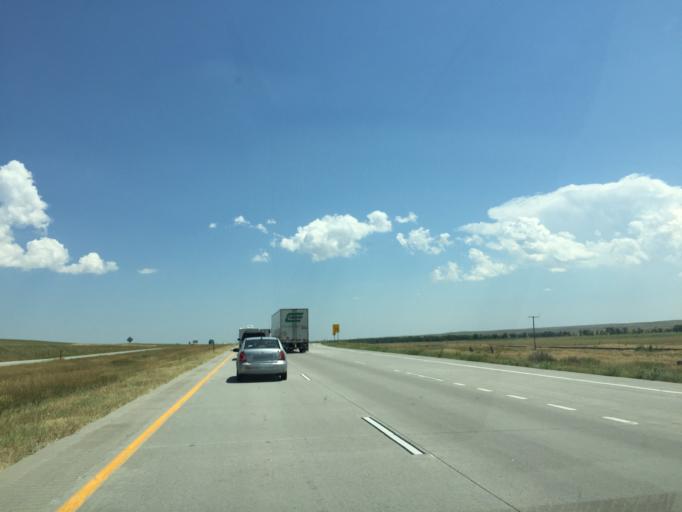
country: US
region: Colorado
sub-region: Lincoln County
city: Limon
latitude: 39.2926
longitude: -103.7979
